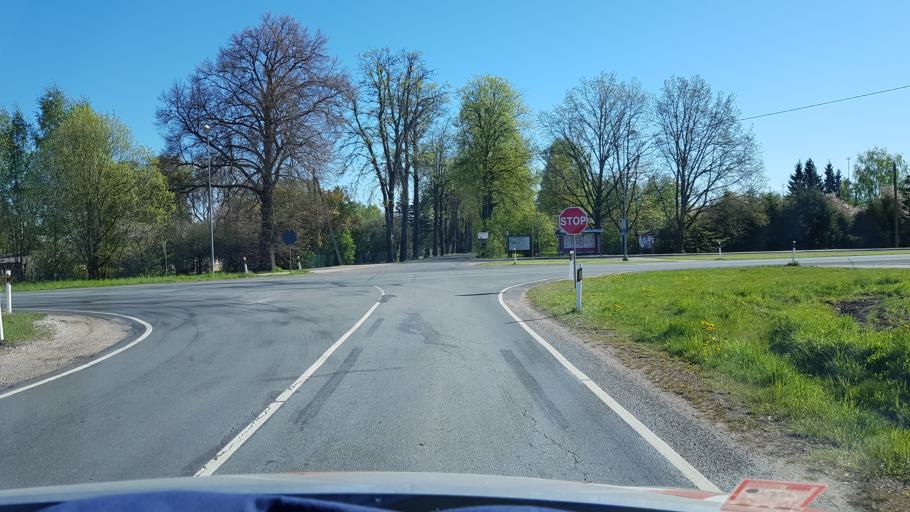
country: EE
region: Polvamaa
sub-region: Polva linn
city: Polva
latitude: 58.1552
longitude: 27.1816
